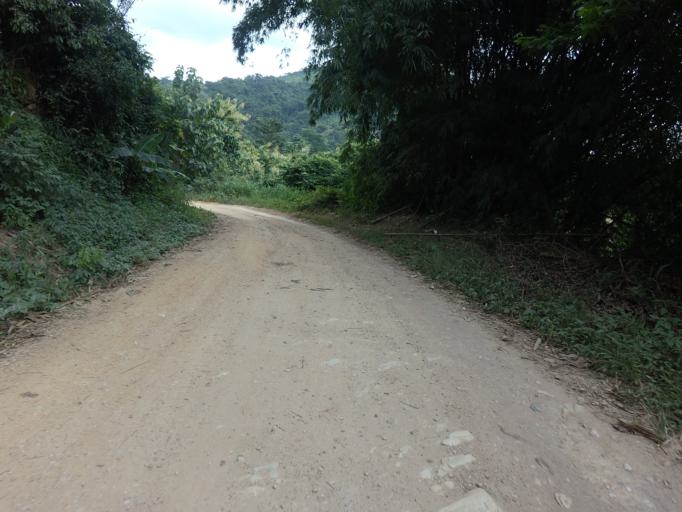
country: GH
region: Volta
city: Kpandu
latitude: 6.8793
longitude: 0.4386
